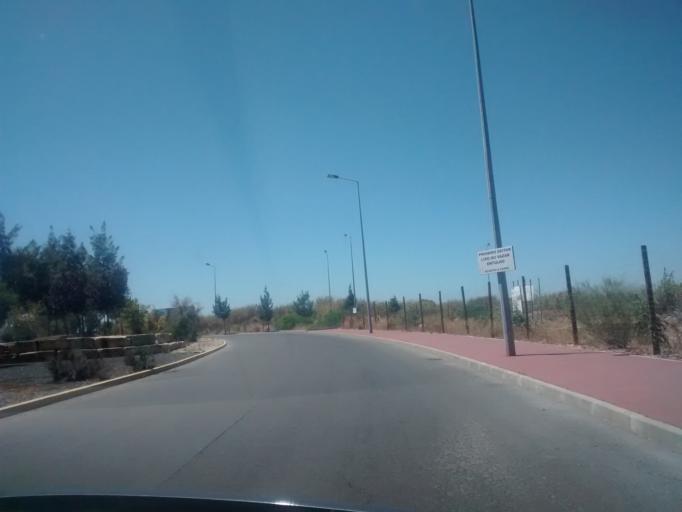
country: PT
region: Faro
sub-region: Vila Real de Santo Antonio
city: Vila Real de Santo Antonio
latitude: 37.2020
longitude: -7.4177
